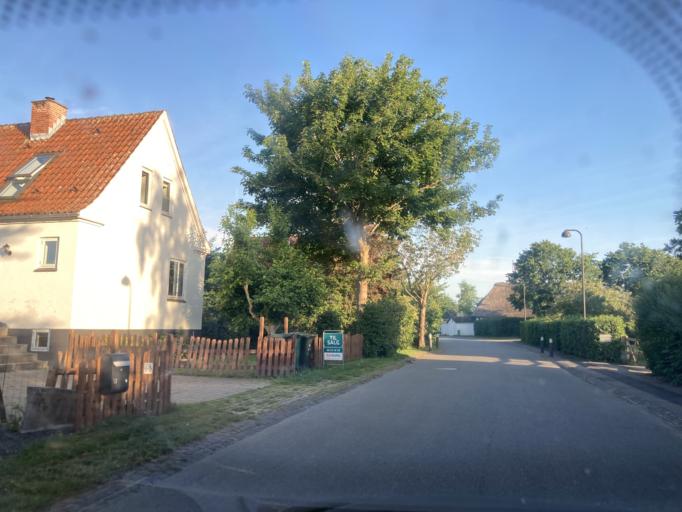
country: DK
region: Zealand
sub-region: Lejre Kommune
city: Lejre
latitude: 55.6481
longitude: 11.9620
